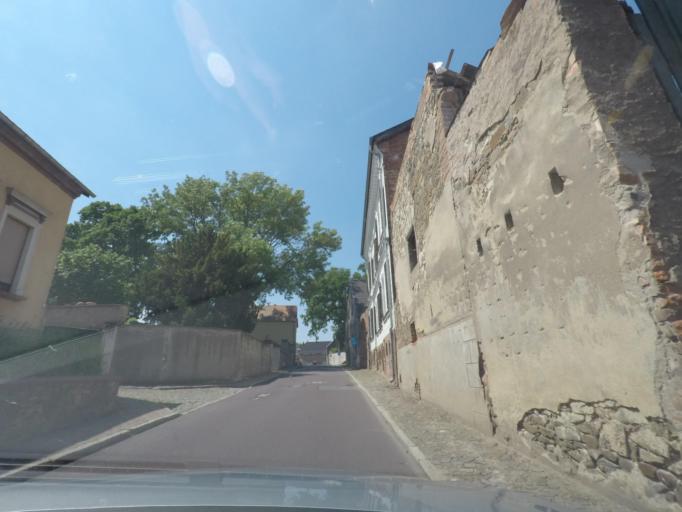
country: DE
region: Saxony-Anhalt
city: Haldensleben I
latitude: 52.2471
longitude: 11.4015
